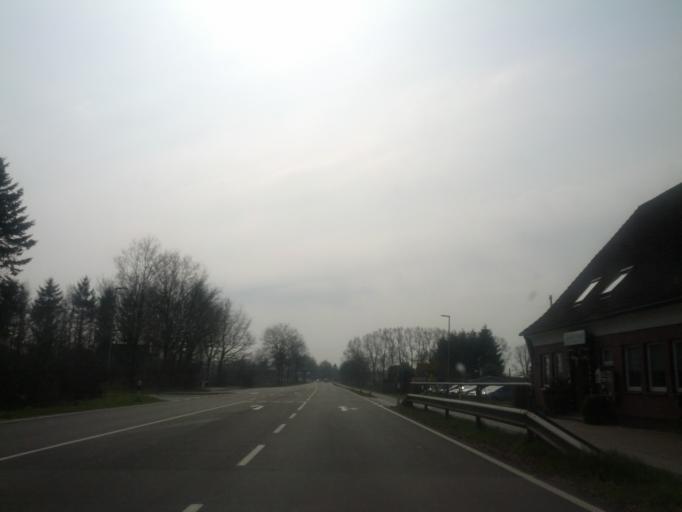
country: DE
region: Lower Saxony
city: Osteel
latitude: 53.5334
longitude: 7.2661
